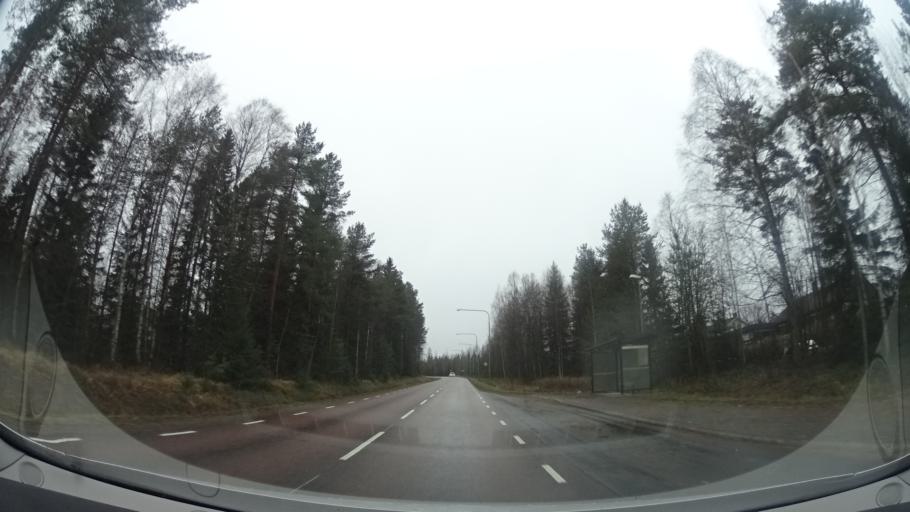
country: SE
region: Vaesterbotten
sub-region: Skelleftea Kommun
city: Skelleftea
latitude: 64.7596
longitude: 21.0182
